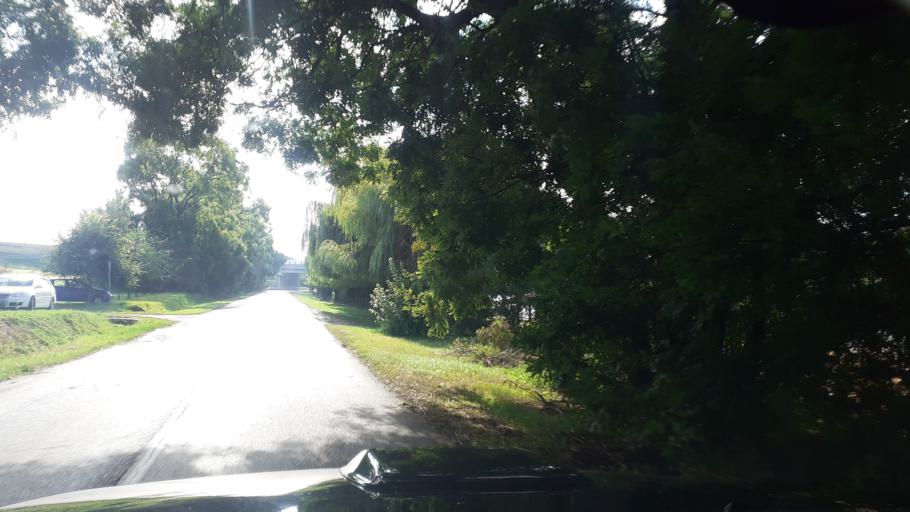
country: HU
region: Fejer
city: Baracs
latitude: 46.9114
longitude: 18.8870
